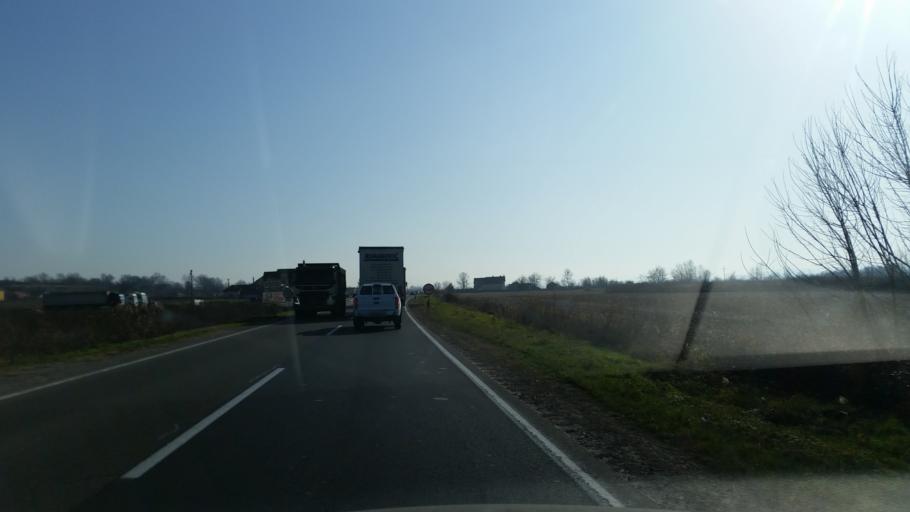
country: RS
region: Central Serbia
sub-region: Belgrade
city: Lazarevac
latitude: 44.3152
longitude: 20.2369
